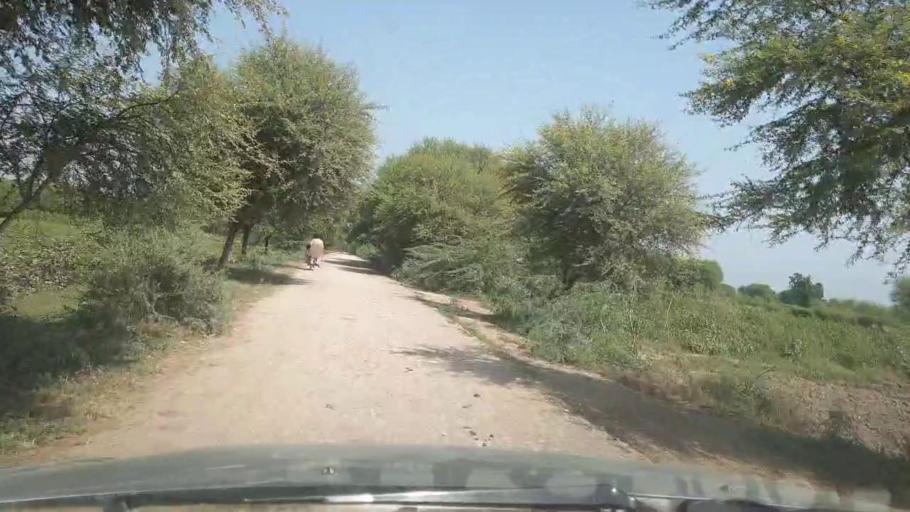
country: PK
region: Sindh
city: Tando Ghulam Ali
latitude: 25.1794
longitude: 68.8744
